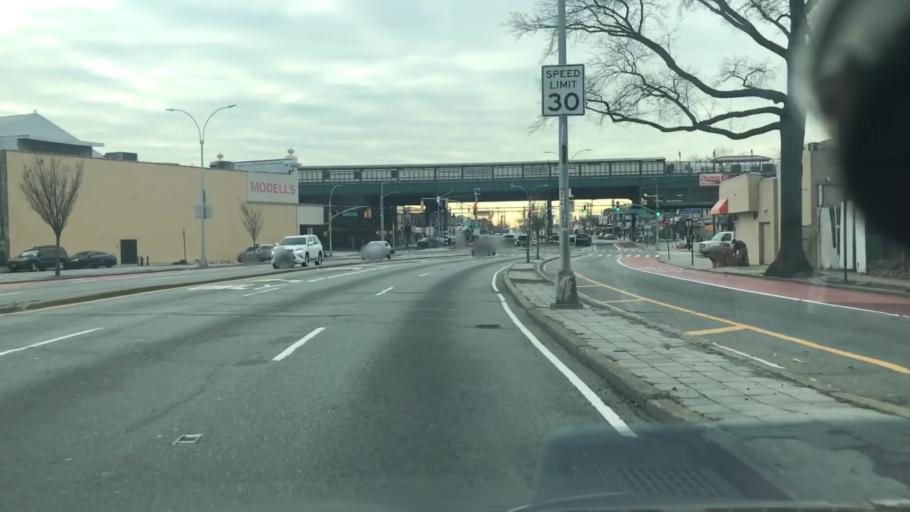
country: US
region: New York
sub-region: Queens County
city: Borough of Queens
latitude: 40.6816
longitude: -73.8449
